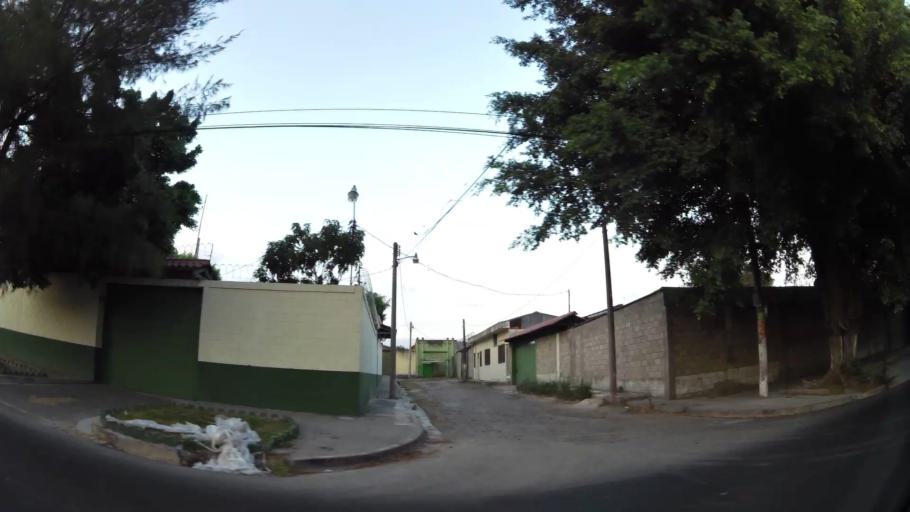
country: SV
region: San Salvador
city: San Salvador
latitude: 13.7098
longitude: -89.1872
